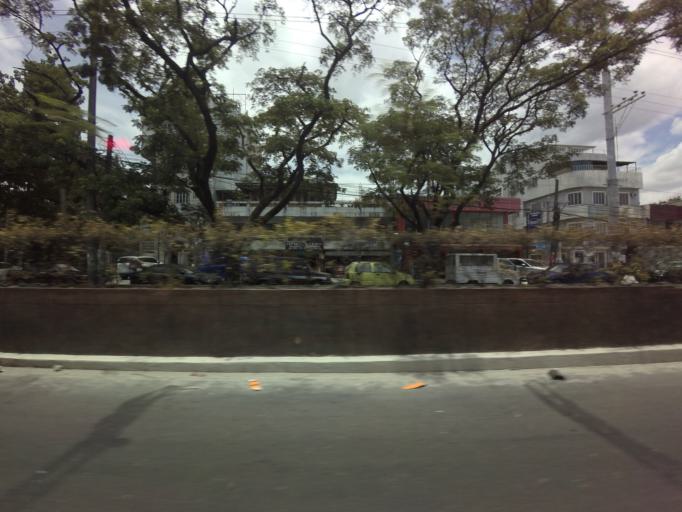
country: PH
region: Metro Manila
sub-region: Marikina
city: Calumpang
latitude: 14.6116
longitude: 121.1032
